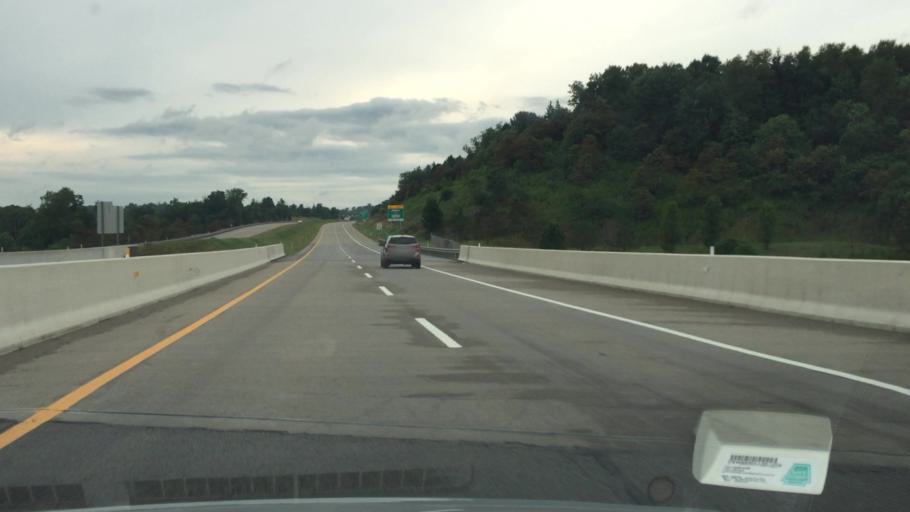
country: US
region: Pennsylvania
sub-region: Allegheny County
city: Imperial
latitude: 40.4660
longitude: -80.2907
